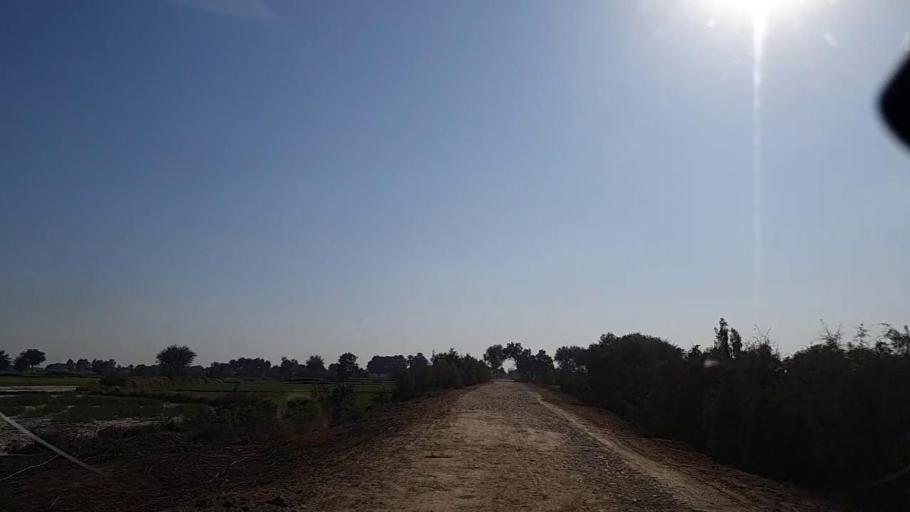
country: PK
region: Sindh
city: Khanpur
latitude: 27.7892
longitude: 69.3699
